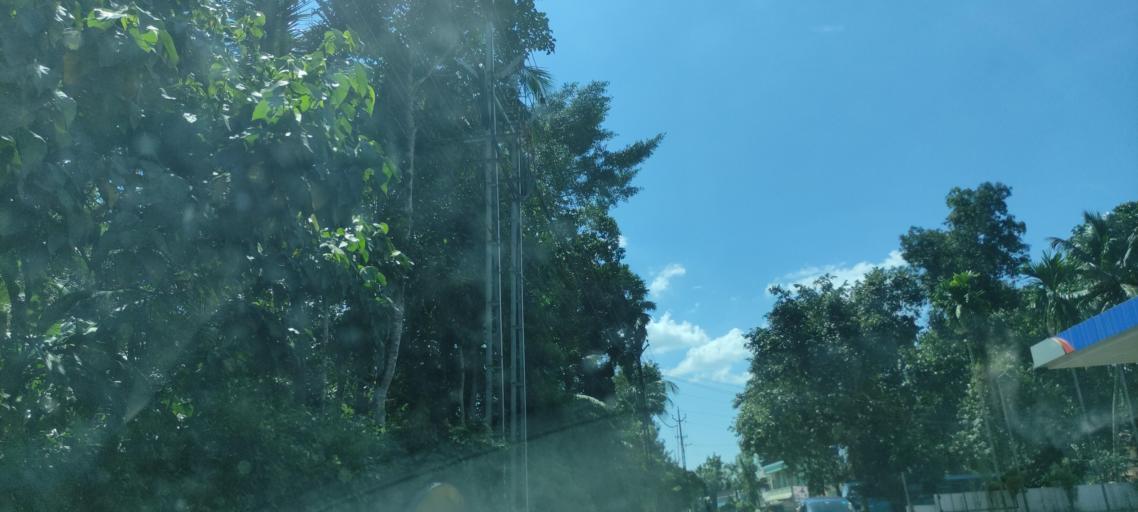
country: IN
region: Kerala
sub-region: Pattanamtitta
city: Adur
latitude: 9.0945
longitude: 76.6879
